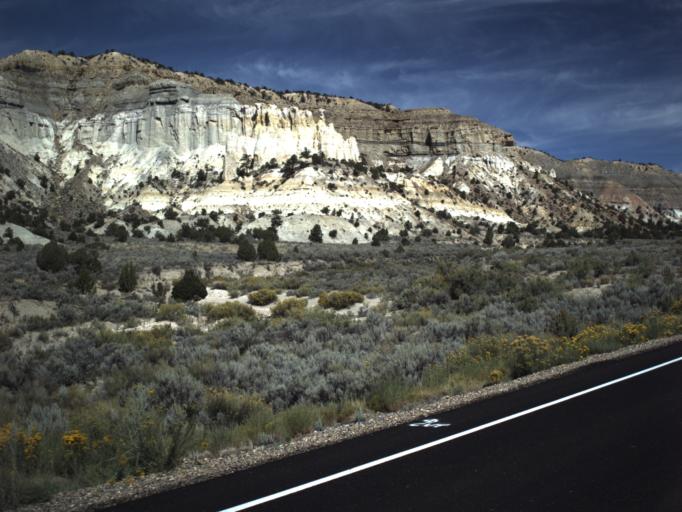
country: US
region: Utah
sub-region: Garfield County
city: Panguitch
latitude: 37.5815
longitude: -111.9850
